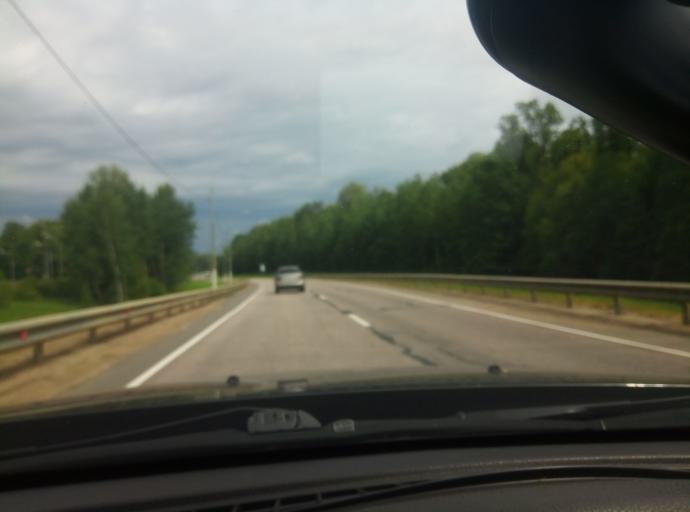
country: RU
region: Tula
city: Leninskiy
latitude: 54.4096
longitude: 37.5020
